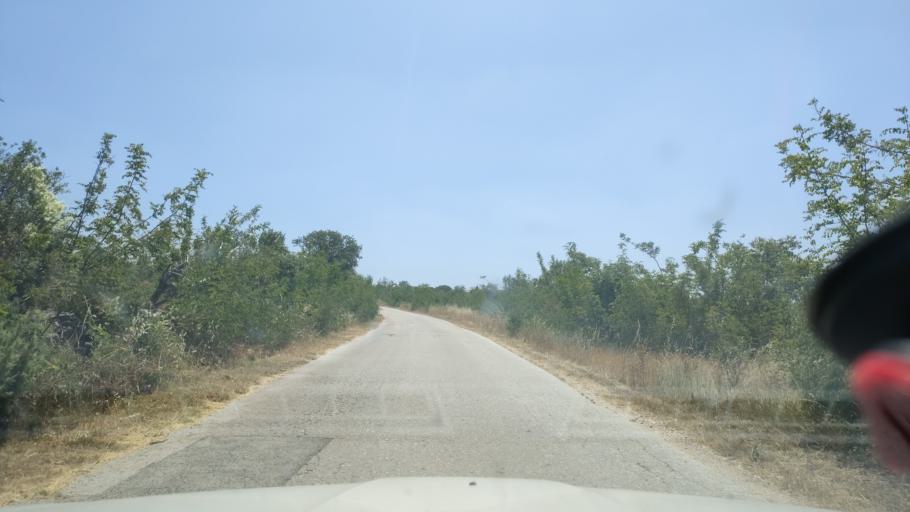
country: HR
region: Sibensko-Kniniska
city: Kistanje
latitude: 43.9632
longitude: 15.8696
